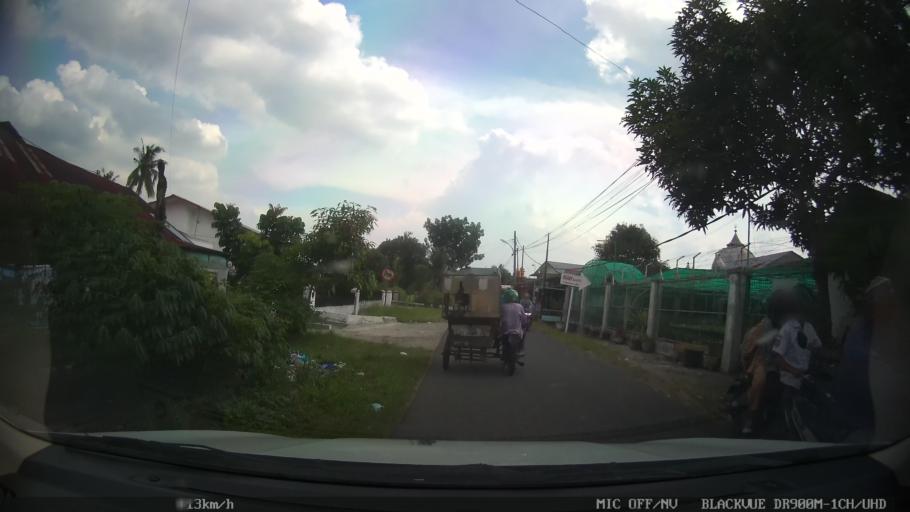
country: ID
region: North Sumatra
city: Binjai
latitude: 3.6165
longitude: 98.4996
